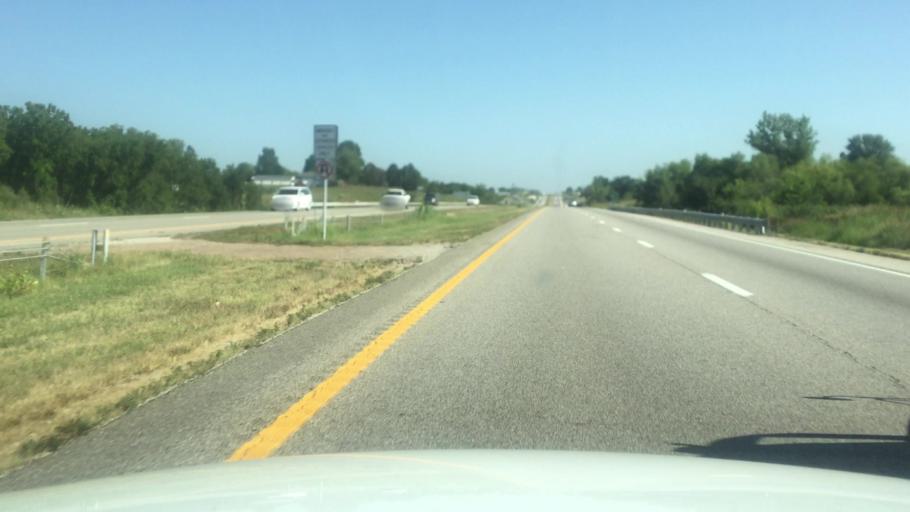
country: US
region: Kansas
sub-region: Doniphan County
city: Elwood
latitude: 39.5883
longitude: -94.7888
